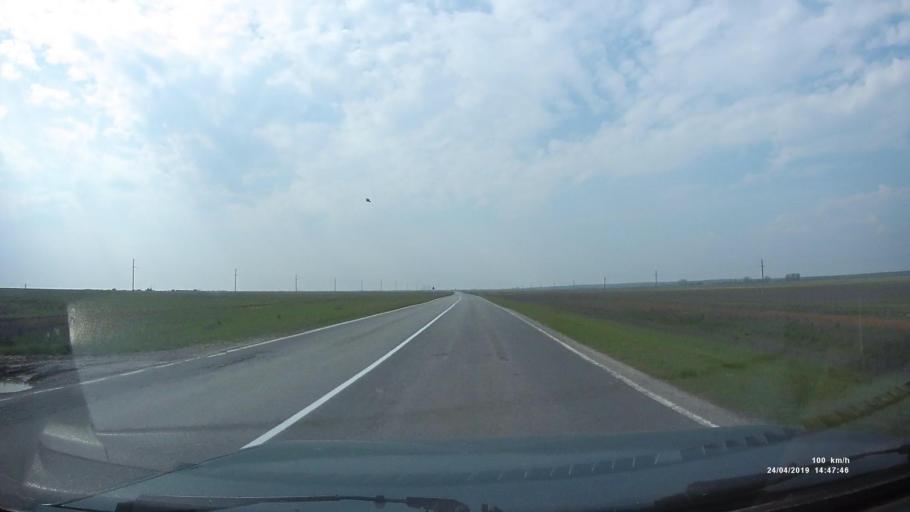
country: RU
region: Rostov
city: Remontnoye
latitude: 46.4948
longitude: 43.7670
